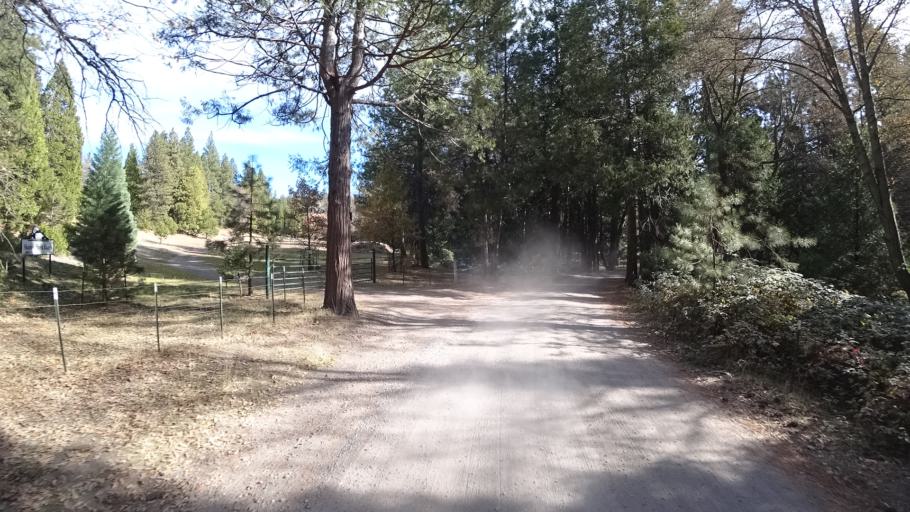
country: US
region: California
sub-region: Siskiyou County
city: Weed
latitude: 41.4342
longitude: -122.4177
